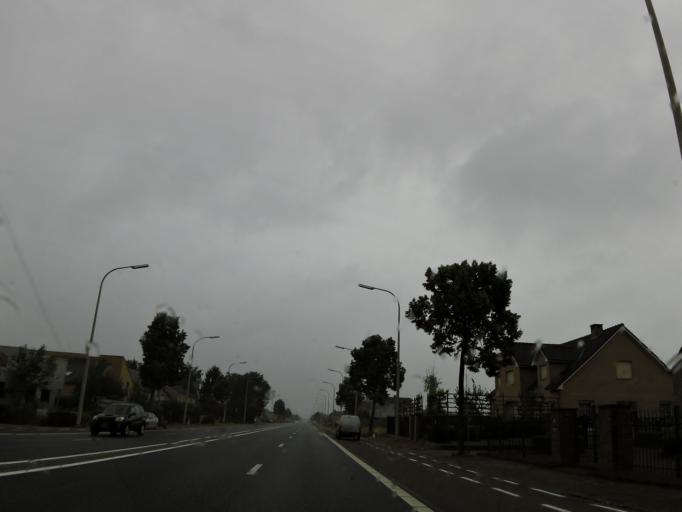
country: NL
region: Limburg
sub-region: Gemeente Stein
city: Berg
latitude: 51.0051
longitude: 5.7245
